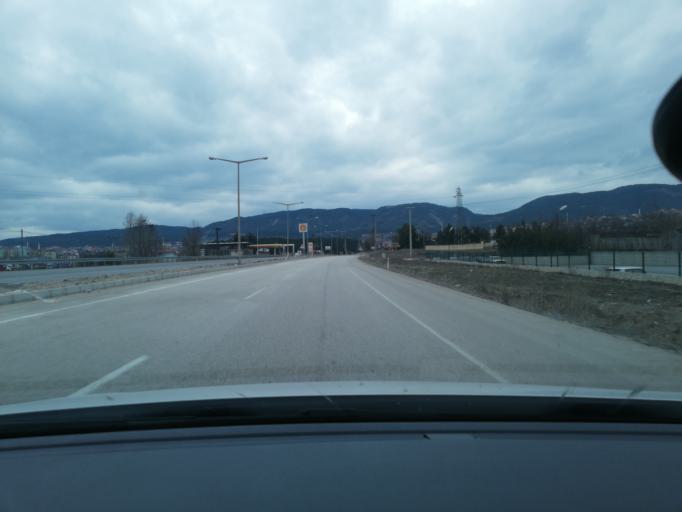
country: TR
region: Bolu
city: Gerede
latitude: 40.7851
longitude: 32.2107
